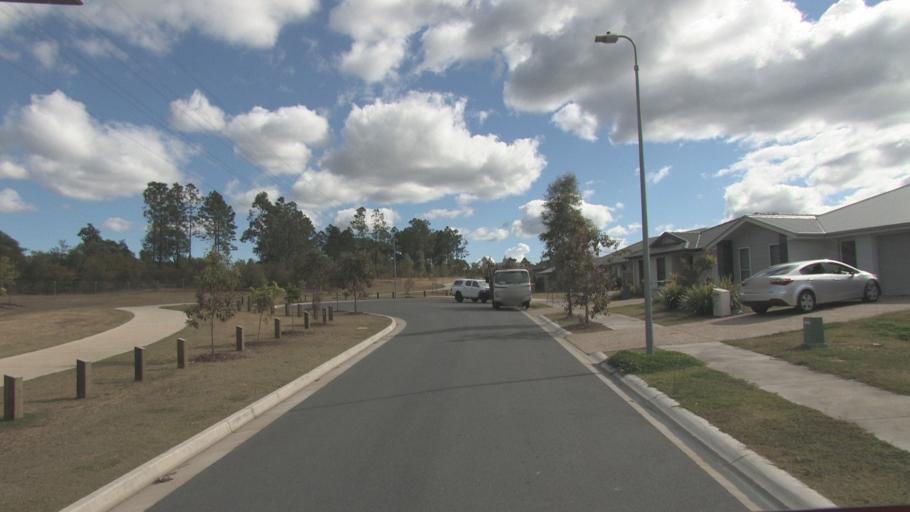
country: AU
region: Queensland
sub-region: Logan
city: Chambers Flat
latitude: -27.8082
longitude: 153.1076
